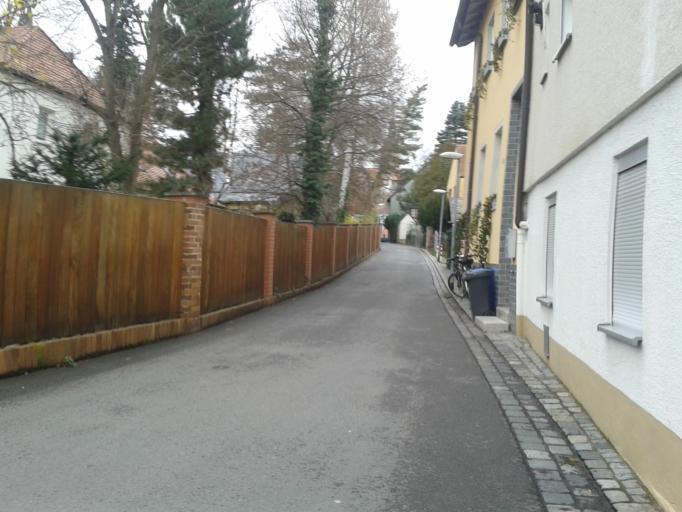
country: DE
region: Bavaria
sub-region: Upper Franconia
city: Bamberg
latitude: 49.8886
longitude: 10.8788
